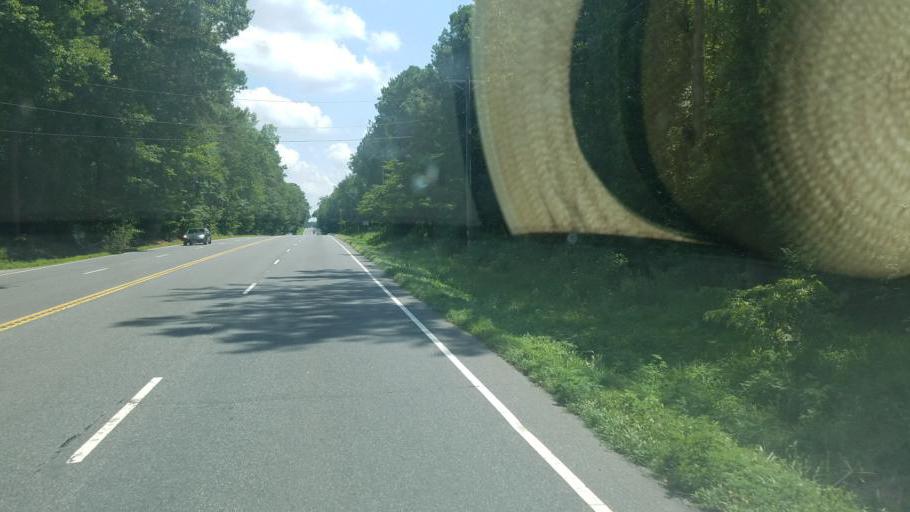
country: US
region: Virginia
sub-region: Isle of Wight County
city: Windsor
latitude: 36.8618
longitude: -76.8227
